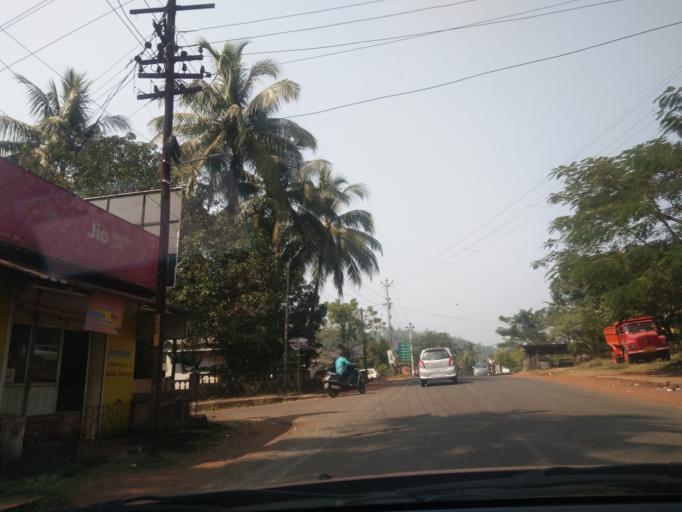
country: IN
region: Goa
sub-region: North Goa
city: Sanquelim
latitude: 15.5573
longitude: 74.0174
